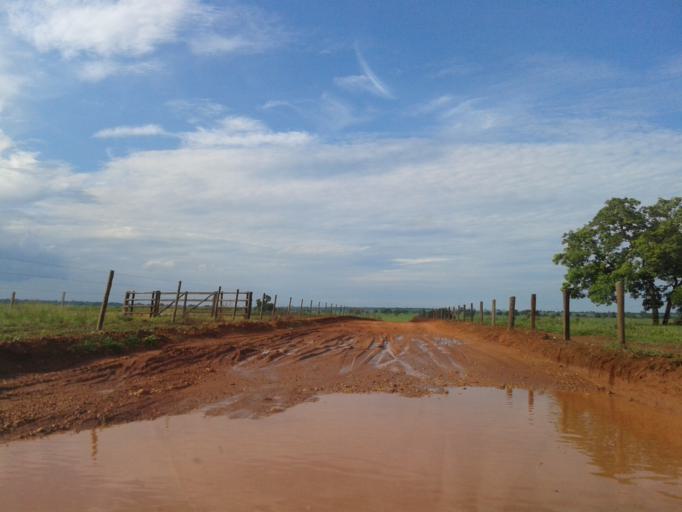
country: BR
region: Minas Gerais
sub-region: Santa Vitoria
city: Santa Vitoria
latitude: -19.1448
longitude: -50.5633
